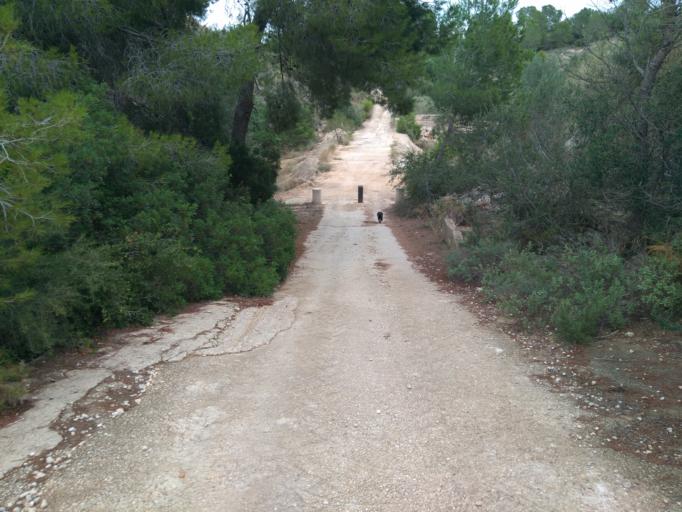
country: ES
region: Valencia
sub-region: Provincia de Valencia
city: Benimodo
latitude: 39.1976
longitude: -0.5751
